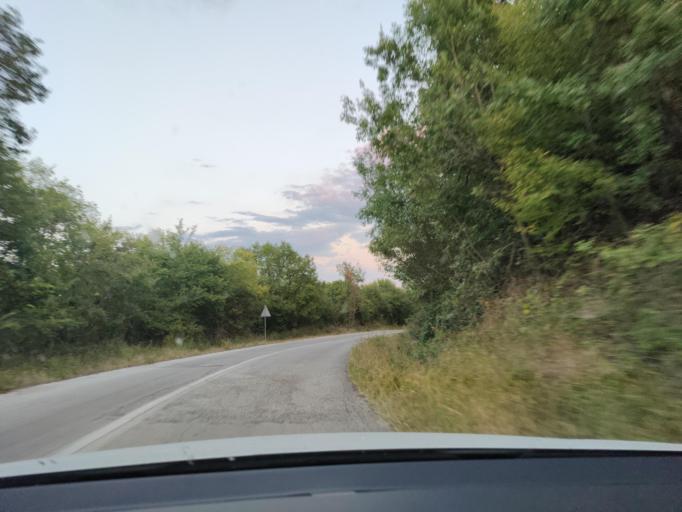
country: GR
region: Central Macedonia
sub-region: Nomos Serron
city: Chrysochorafa
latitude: 41.1801
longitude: 23.1608
